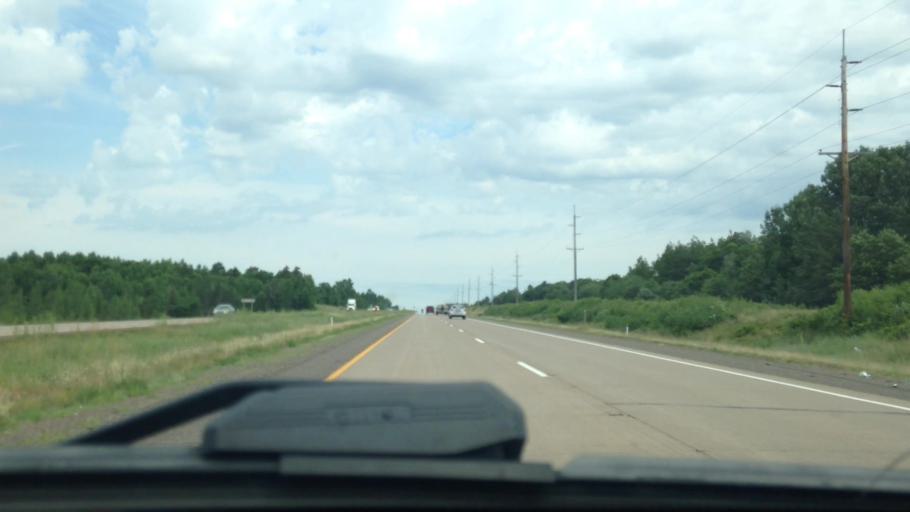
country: US
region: Wisconsin
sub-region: Douglas County
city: Lake Nebagamon
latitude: 46.2225
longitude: -91.8000
